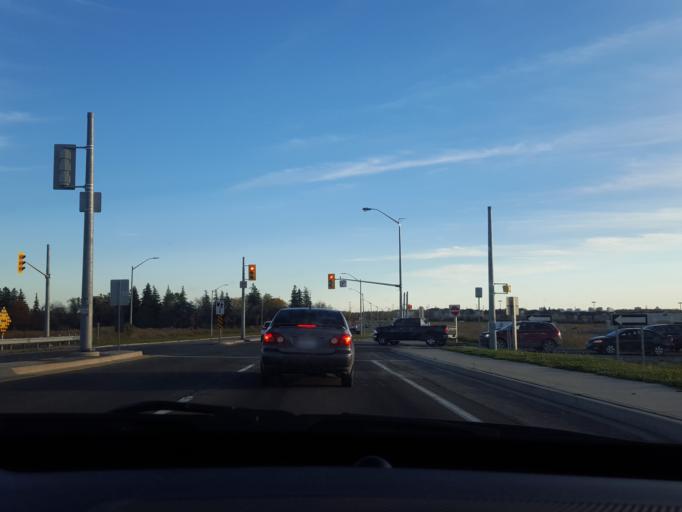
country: CA
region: Ontario
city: Markham
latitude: 43.8737
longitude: -79.2130
